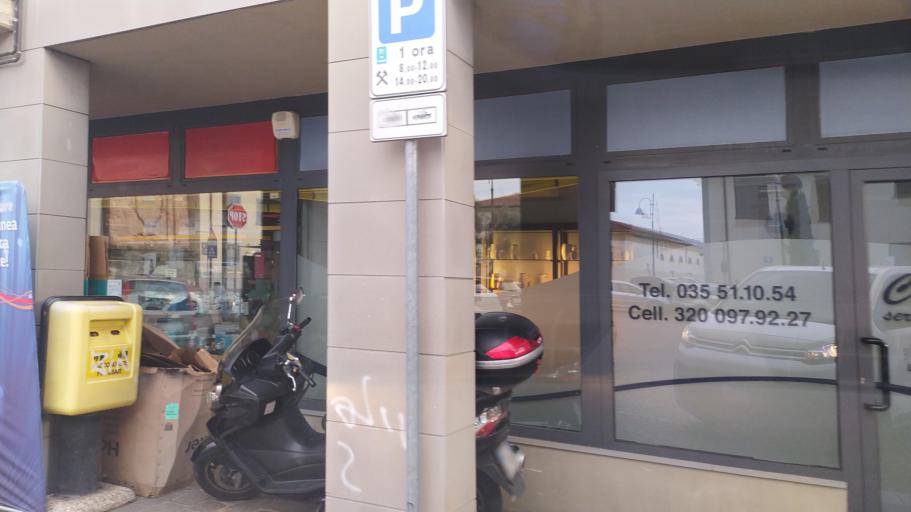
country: IT
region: Lombardy
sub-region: Provincia di Bergamo
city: Lallio
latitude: 45.6773
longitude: 9.6281
